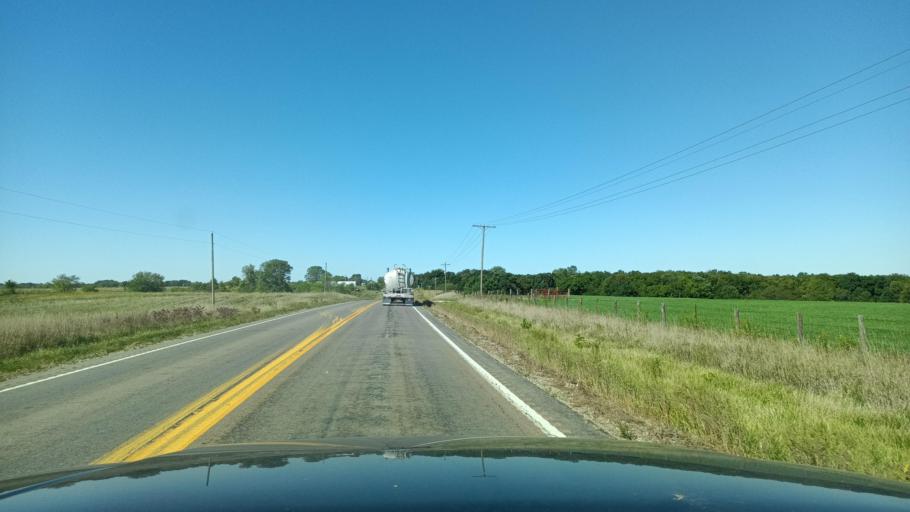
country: US
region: Missouri
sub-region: Scotland County
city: Memphis
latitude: 40.4538
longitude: -92.0123
